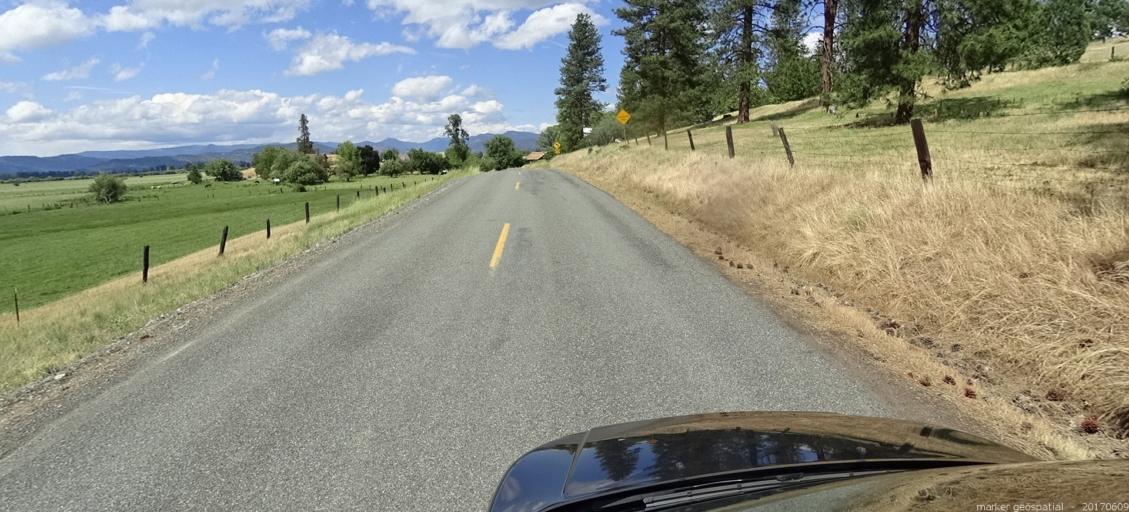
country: US
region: California
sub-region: Siskiyou County
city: Yreka
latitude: 41.4784
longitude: -122.8777
